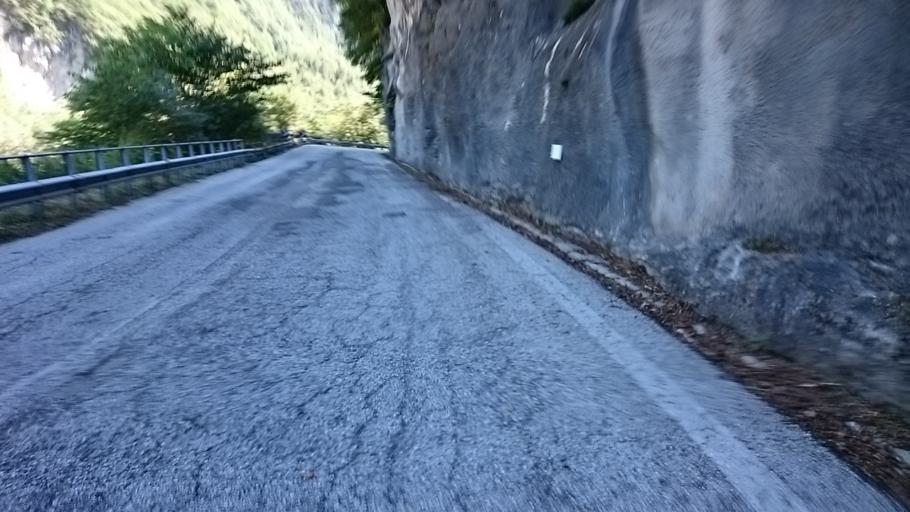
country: IT
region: Veneto
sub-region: Provincia di Belluno
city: Ospitale di Cadore
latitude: 46.3108
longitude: 12.3236
